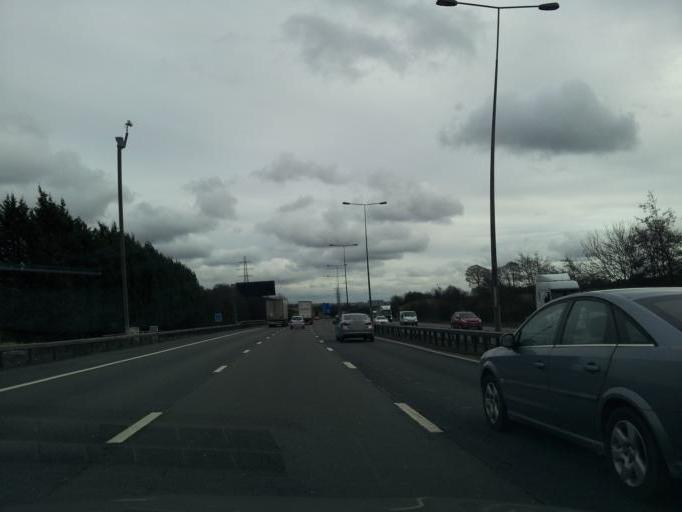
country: GB
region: England
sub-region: Staffordshire
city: Newcastle under Lyme
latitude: 52.9880
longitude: -2.2554
